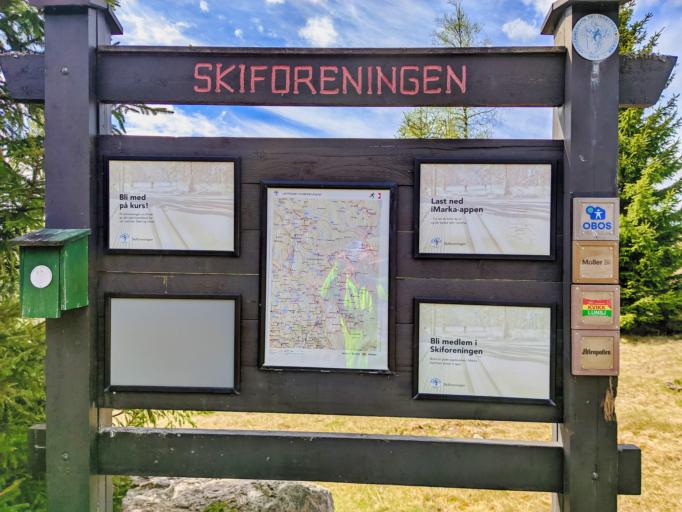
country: NO
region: Akershus
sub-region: Nannestad
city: Teigebyen
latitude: 60.2010
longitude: 10.9152
